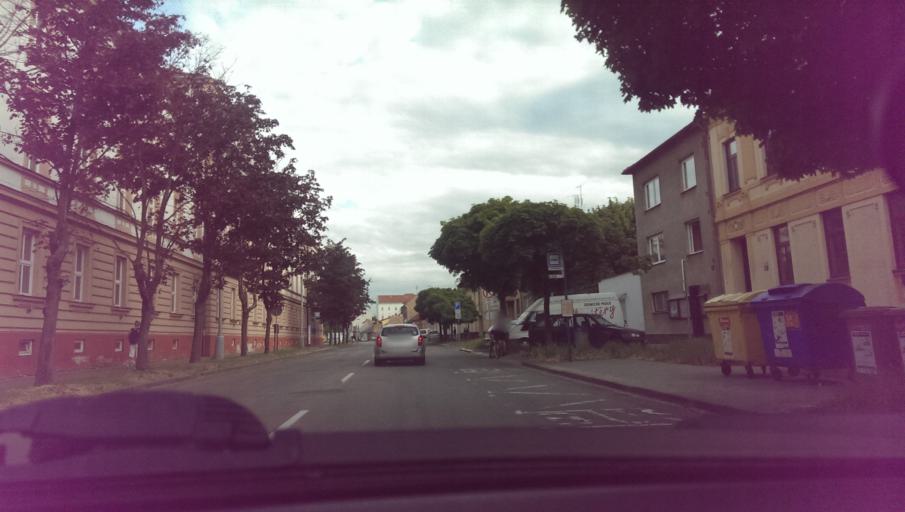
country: CZ
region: Zlin
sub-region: Okres Kromeriz
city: Kromeriz
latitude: 49.2933
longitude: 17.3910
